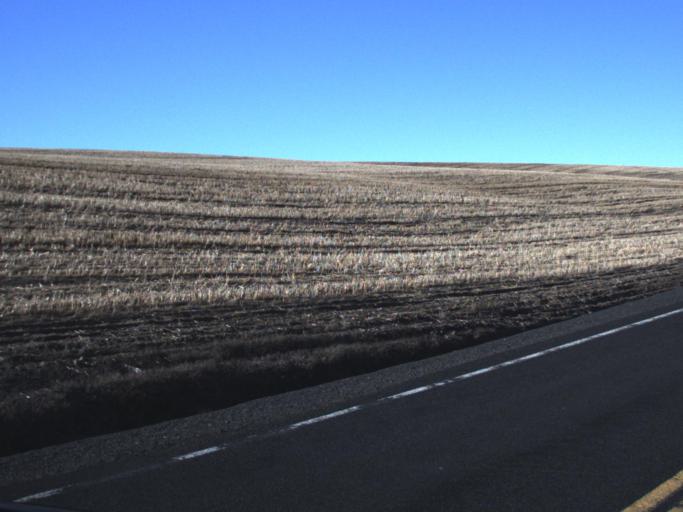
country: US
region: Washington
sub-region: Adams County
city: Ritzville
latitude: 46.9982
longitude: -118.3465
